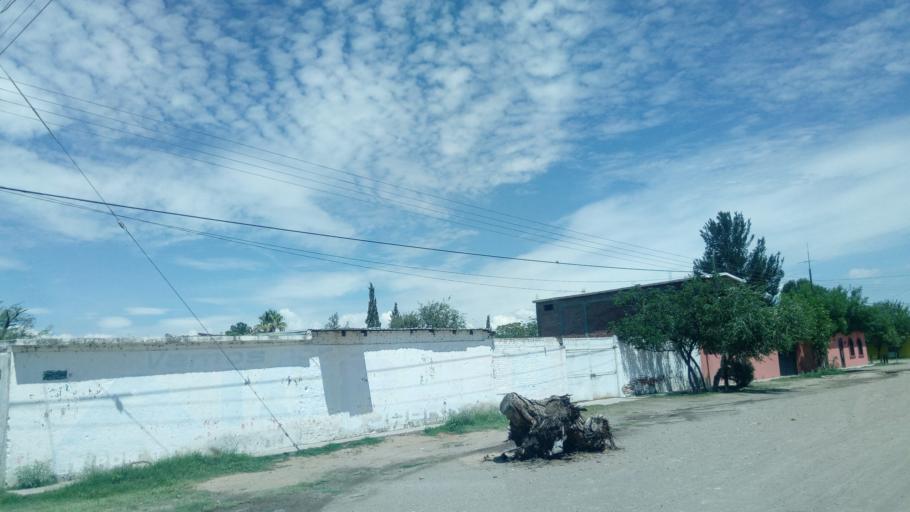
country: MX
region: Durango
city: Victoria de Durango
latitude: 24.0181
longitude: -104.5900
